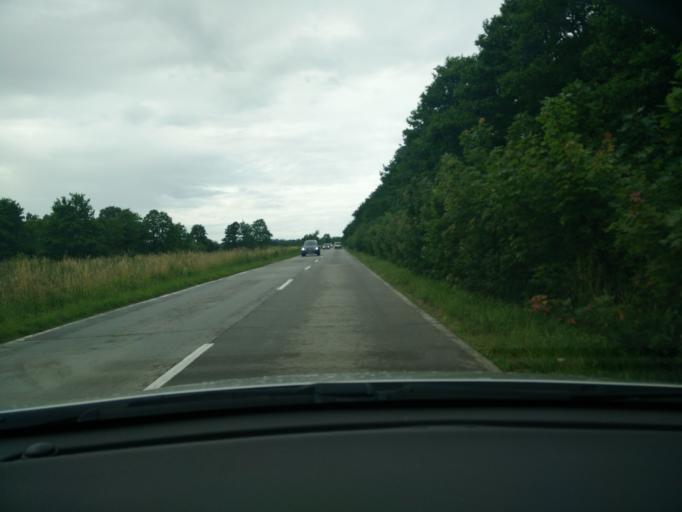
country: PL
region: Pomeranian Voivodeship
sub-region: Powiat pucki
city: Mrzezino
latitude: 54.6150
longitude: 18.4483
